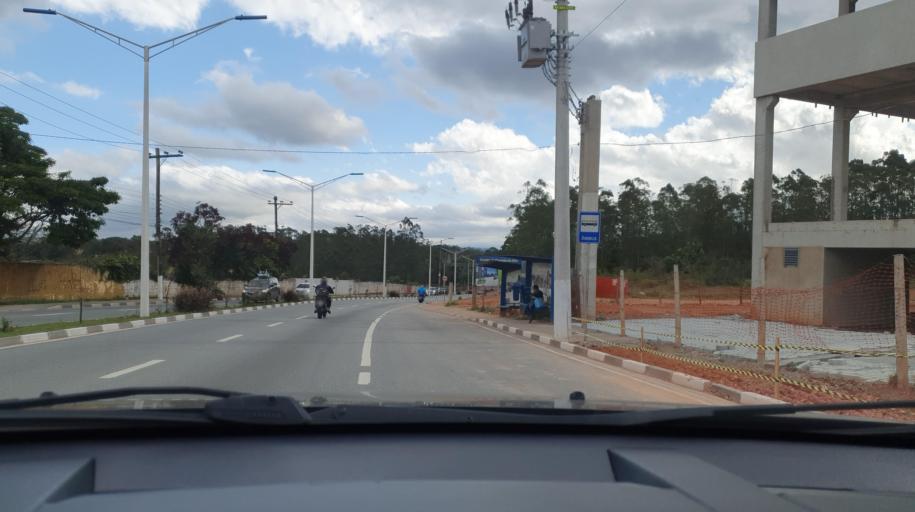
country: BR
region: Sao Paulo
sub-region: Cotia
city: Cotia
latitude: -23.6161
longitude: -46.9718
